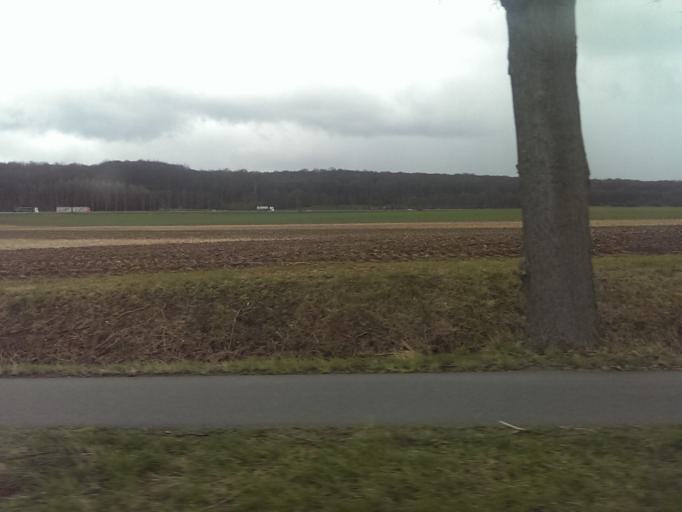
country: DE
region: Lower Saxony
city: Schellerten
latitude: 52.1366
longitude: 10.0354
